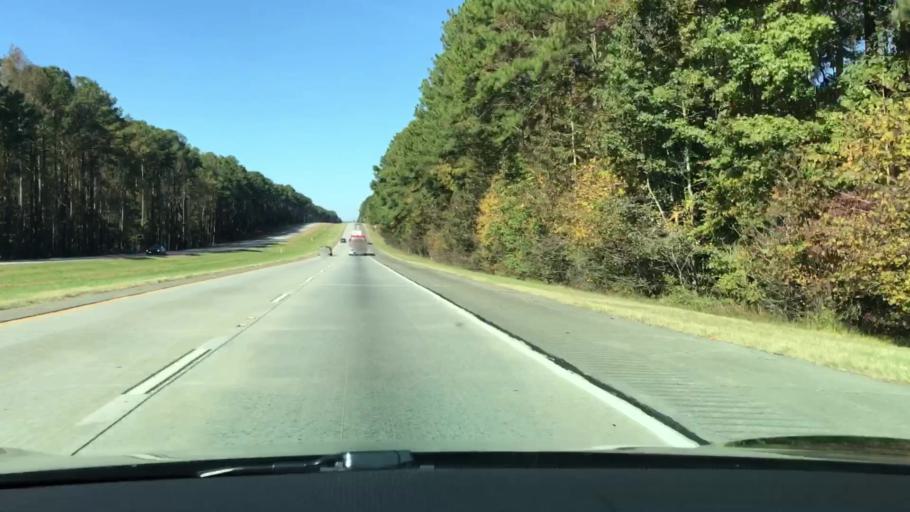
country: US
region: Georgia
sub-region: Taliaferro County
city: Crawfordville
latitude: 33.5033
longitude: -82.8273
